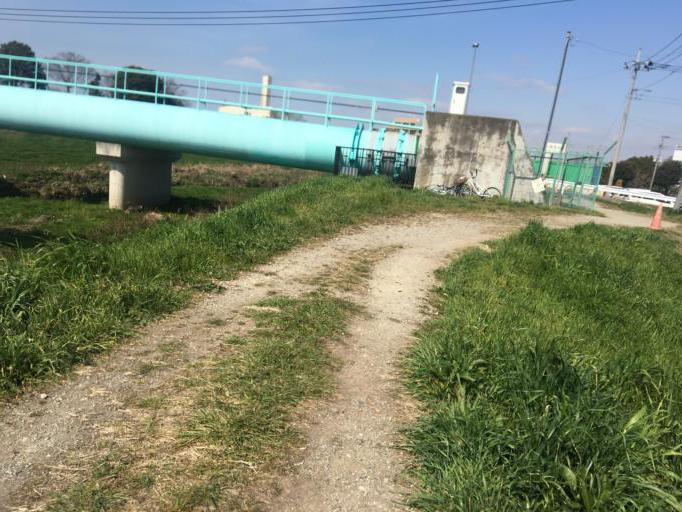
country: JP
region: Saitama
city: Oi
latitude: 35.8675
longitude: 139.5505
